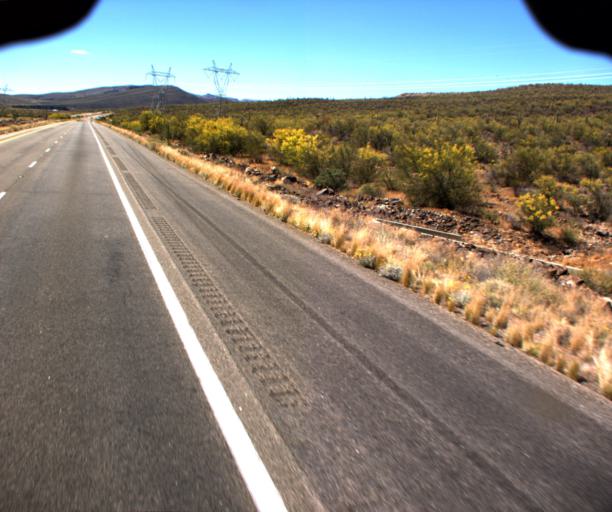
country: US
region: Arizona
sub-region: Yavapai County
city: Bagdad
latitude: 34.5249
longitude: -113.4261
